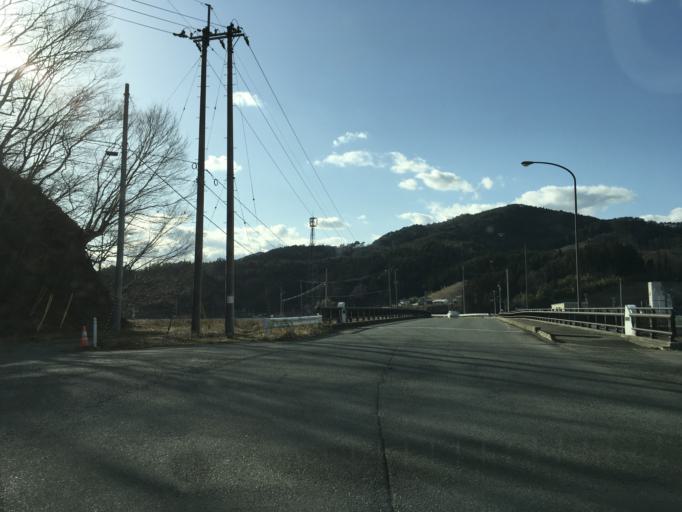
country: JP
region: Iwate
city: Ofunato
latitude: 39.0308
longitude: 141.6039
